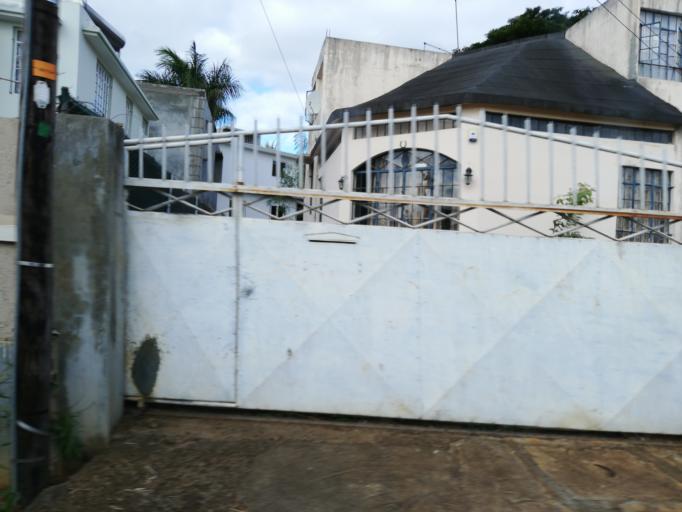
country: MU
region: Black River
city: Petite Riviere
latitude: -20.2195
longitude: 57.4606
